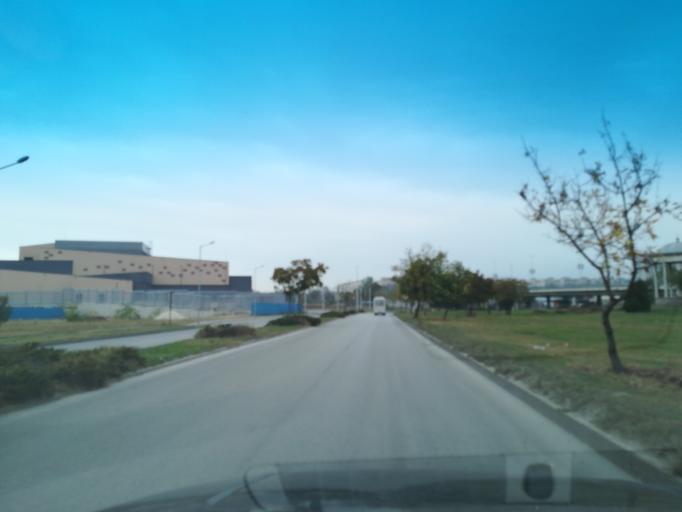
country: BG
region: Plovdiv
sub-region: Obshtina Plovdiv
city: Plovdiv
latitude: 42.1470
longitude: 24.7990
